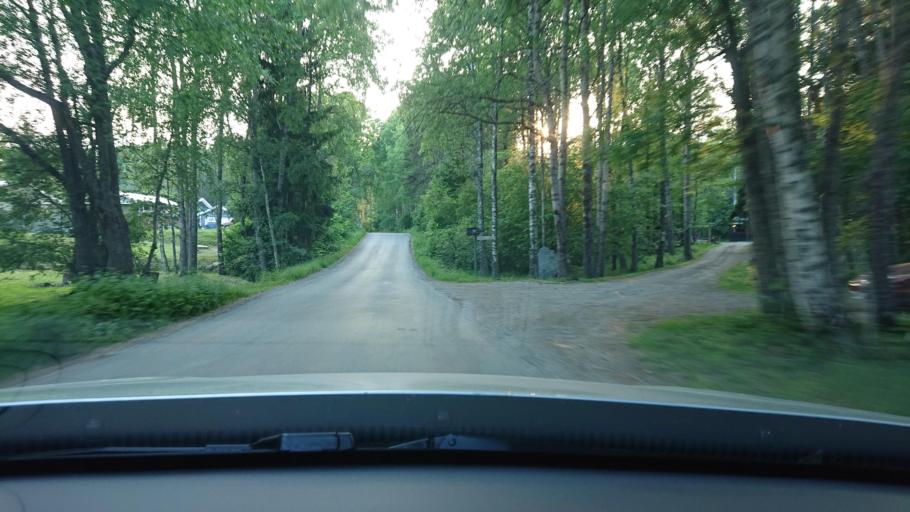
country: SE
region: Stockholm
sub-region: Osterakers Kommun
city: Akersberga
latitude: 59.5024
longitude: 18.3491
